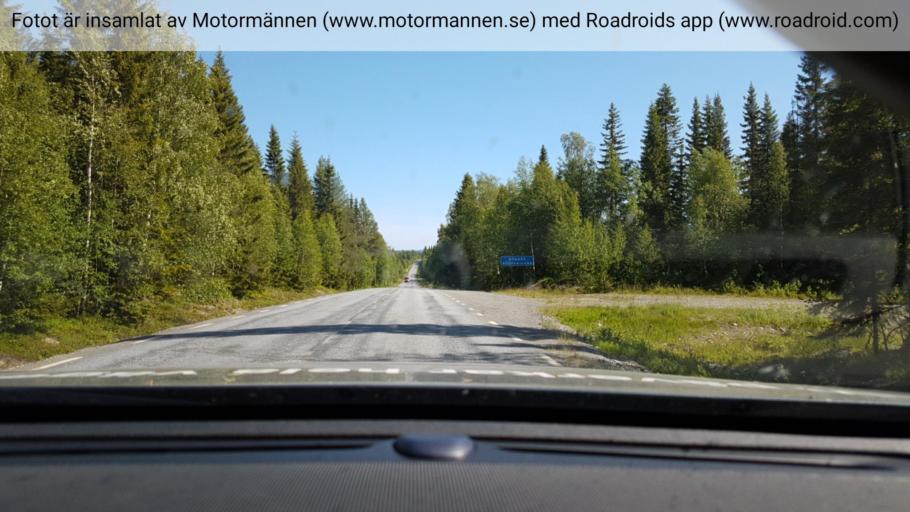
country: SE
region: Vaesterbotten
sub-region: Vilhelmina Kommun
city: Sjoberg
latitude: 64.7785
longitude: 16.1267
